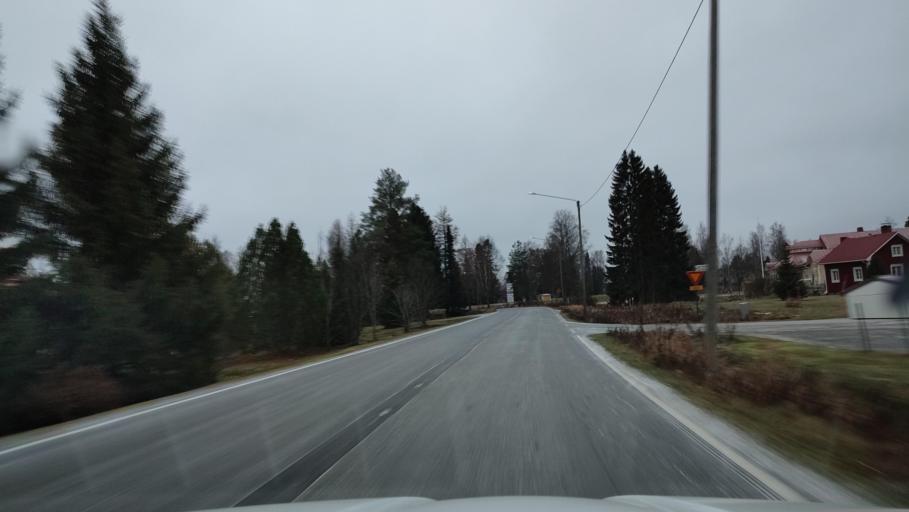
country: FI
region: Southern Ostrobothnia
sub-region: Suupohja
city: Karijoki
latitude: 62.2330
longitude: 21.6477
